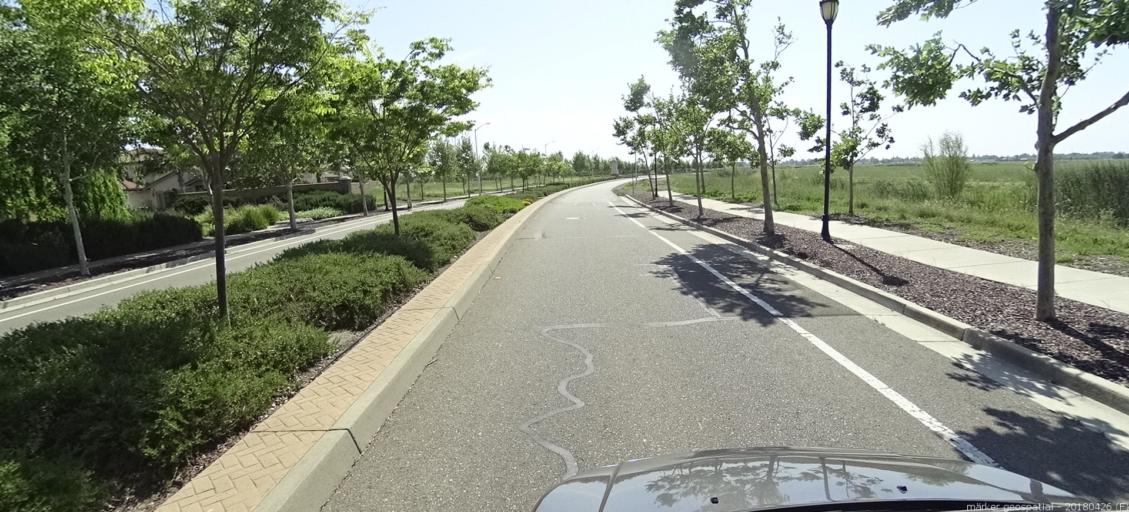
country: US
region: California
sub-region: Yolo County
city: West Sacramento
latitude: 38.5236
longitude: -121.5738
